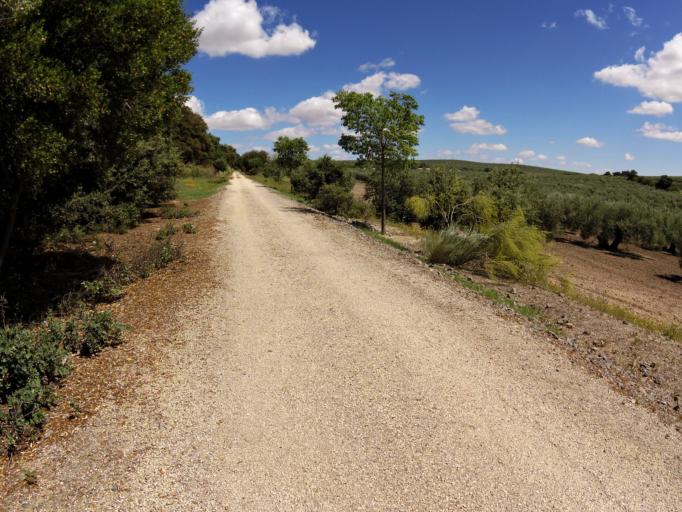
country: ES
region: Andalusia
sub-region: Provincia de Jaen
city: Alcaudete
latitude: 37.6569
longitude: -4.0622
